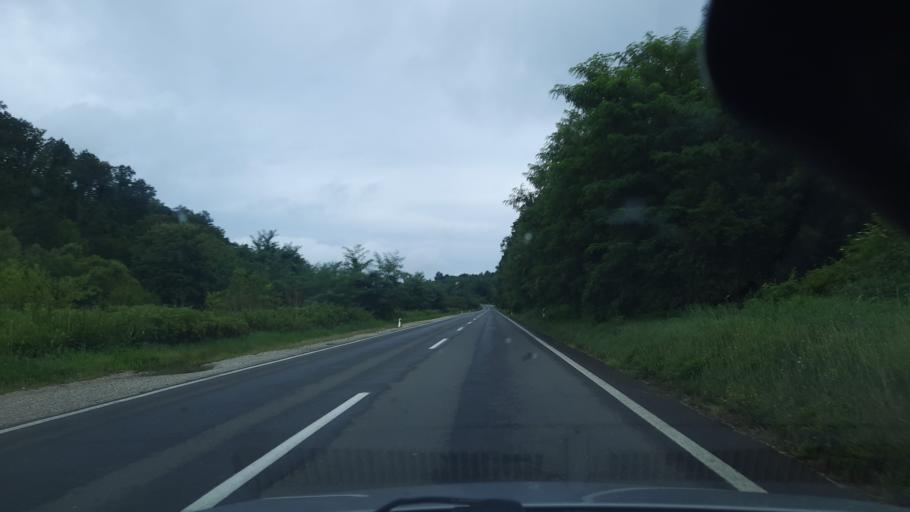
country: RS
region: Central Serbia
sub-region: Sumadijski Okrug
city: Knic
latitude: 43.9584
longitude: 20.8070
